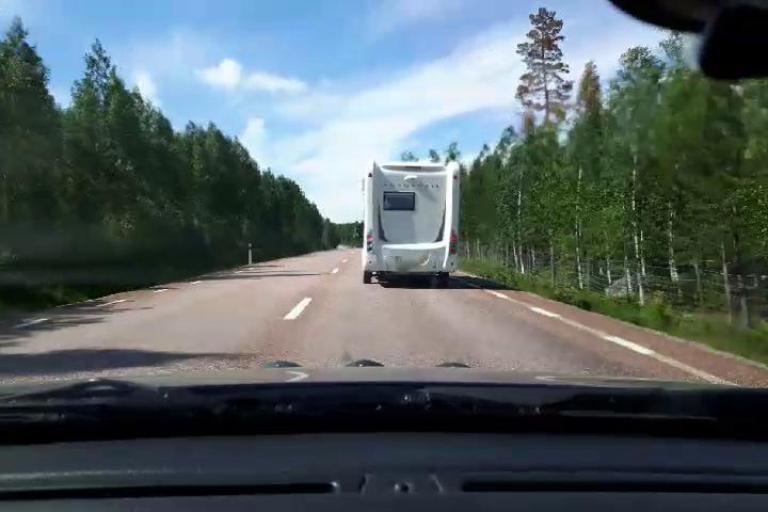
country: SE
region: Gaevleborg
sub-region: Bollnas Kommun
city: Kilafors
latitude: 61.2121
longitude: 16.7382
